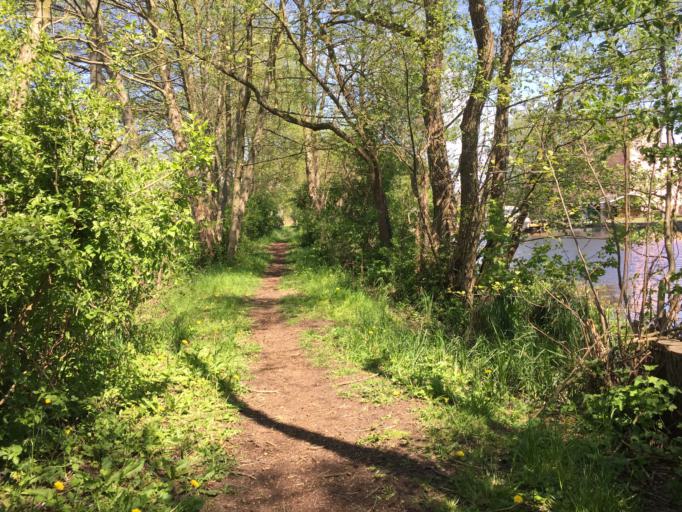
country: DE
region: Brandenburg
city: Melchow
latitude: 52.8460
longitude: 13.6808
